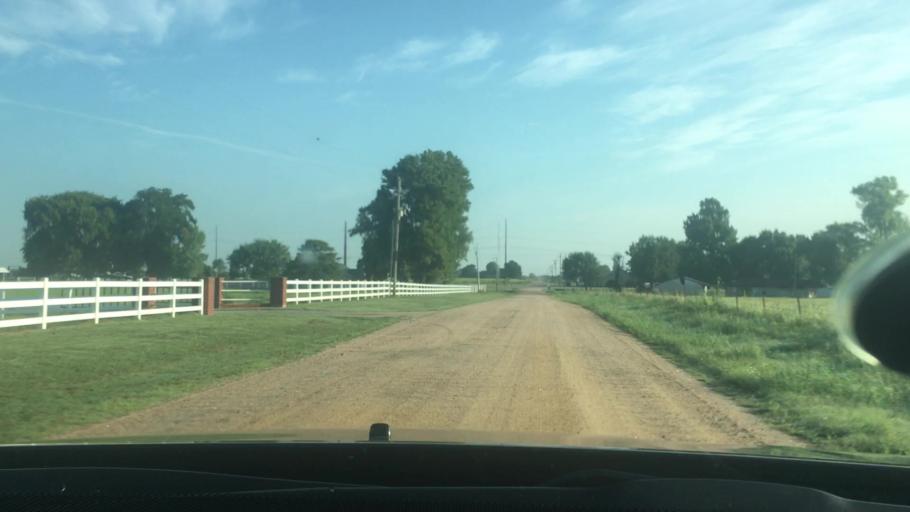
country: US
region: Oklahoma
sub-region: Pontotoc County
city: Ada
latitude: 34.8224
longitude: -96.7747
